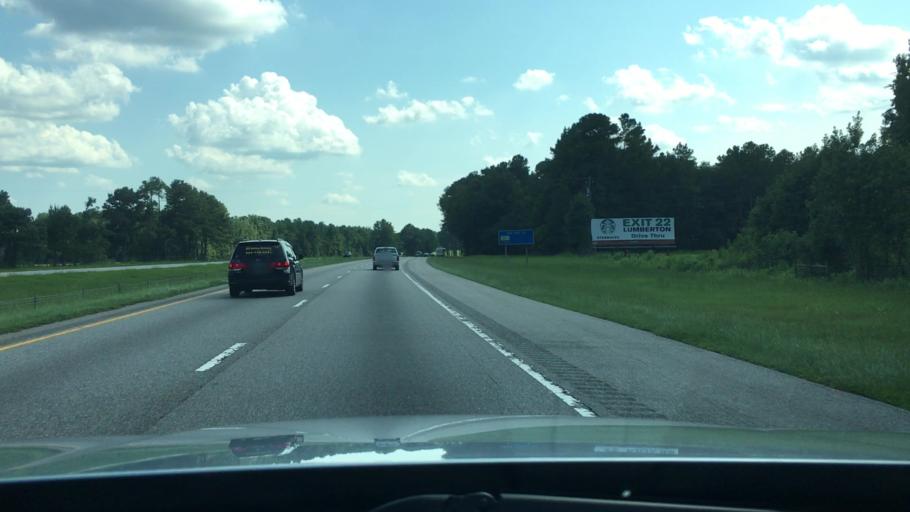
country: US
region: North Carolina
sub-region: Robeson County
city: Saint Pauls
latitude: 34.8407
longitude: -78.9735
